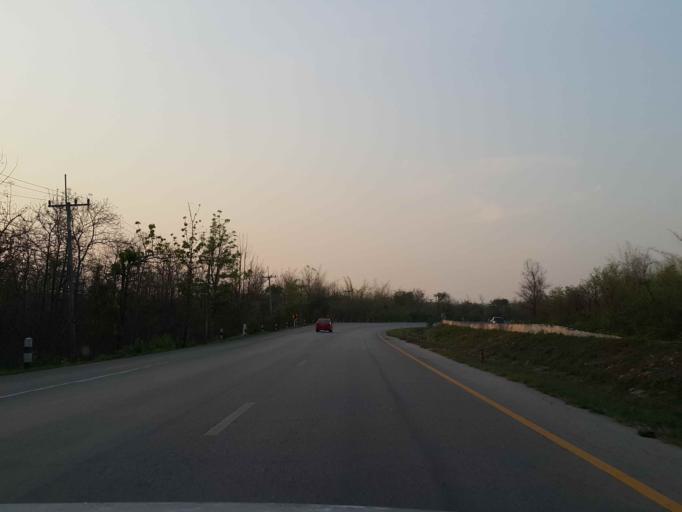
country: TH
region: Lampang
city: Sop Prap
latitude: 17.9663
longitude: 99.3529
